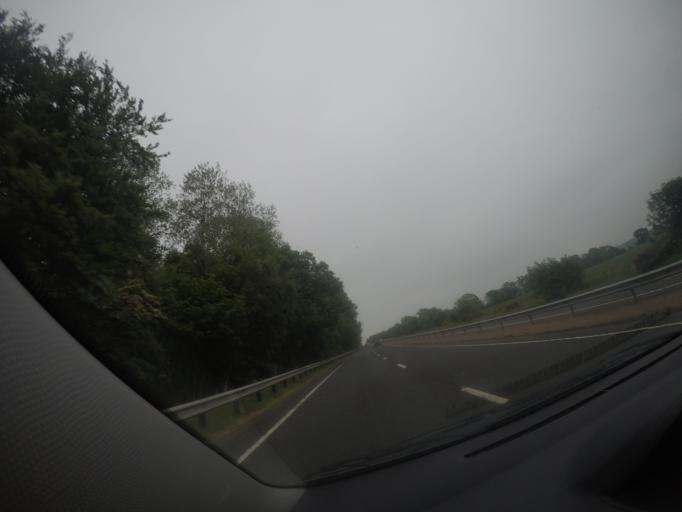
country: GB
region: Scotland
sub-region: Angus
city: Brechin
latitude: 56.7227
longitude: -2.7549
